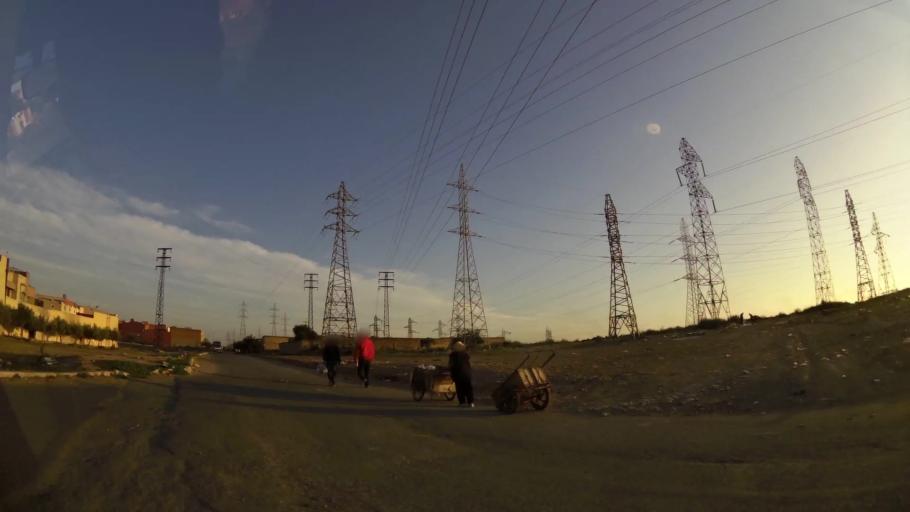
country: MA
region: Oriental
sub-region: Oujda-Angad
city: Oujda
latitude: 34.7094
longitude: -1.9157
